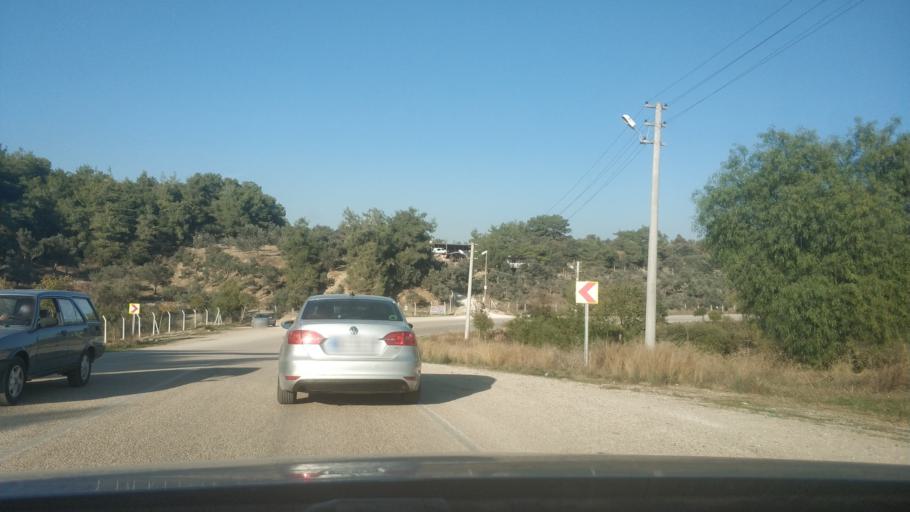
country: TR
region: Adana
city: Adana
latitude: 37.1022
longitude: 35.2917
